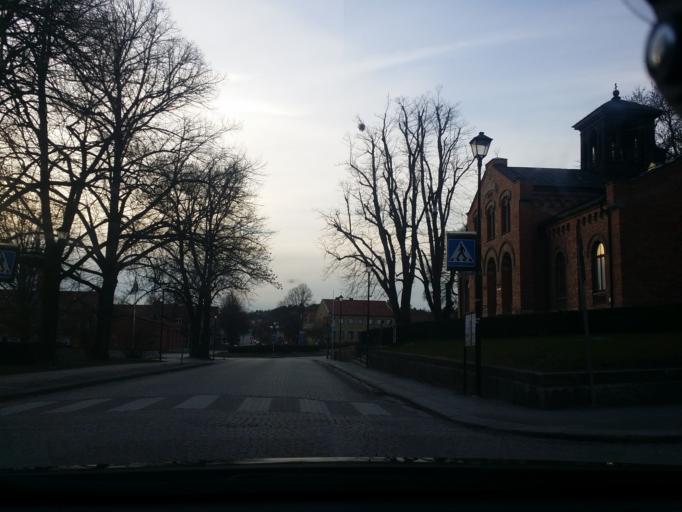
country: SE
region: Uppsala
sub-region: Enkopings Kommun
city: Enkoping
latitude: 59.6375
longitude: 17.0806
